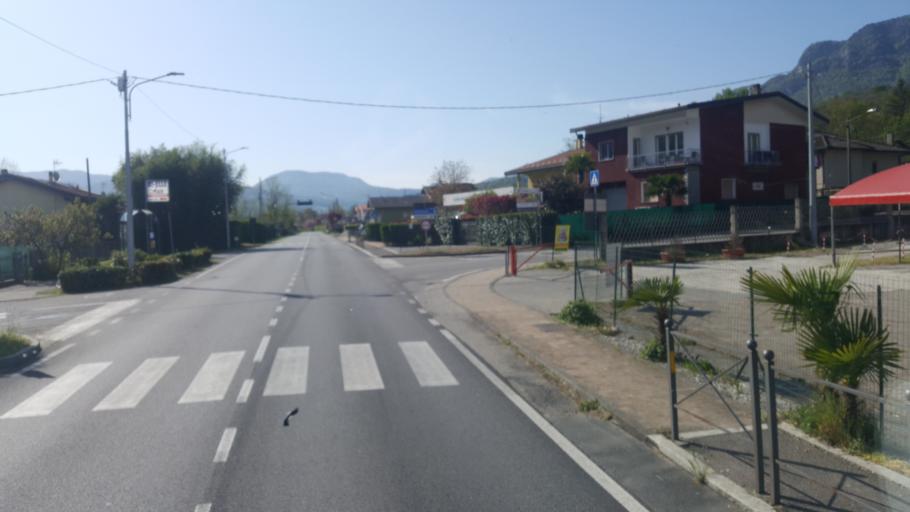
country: IT
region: Lombardy
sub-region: Provincia di Varese
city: Mesenzana
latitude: 45.9630
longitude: 8.7545
